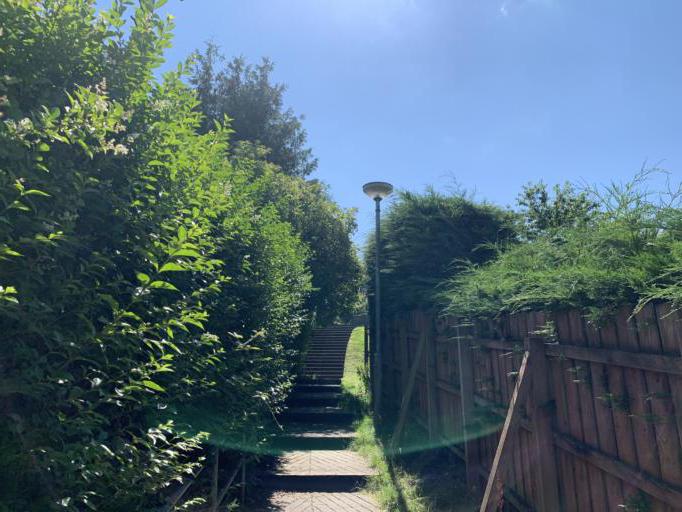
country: GB
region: Scotland
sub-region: East Renfrewshire
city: Clarkston
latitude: 55.7884
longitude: -4.2820
